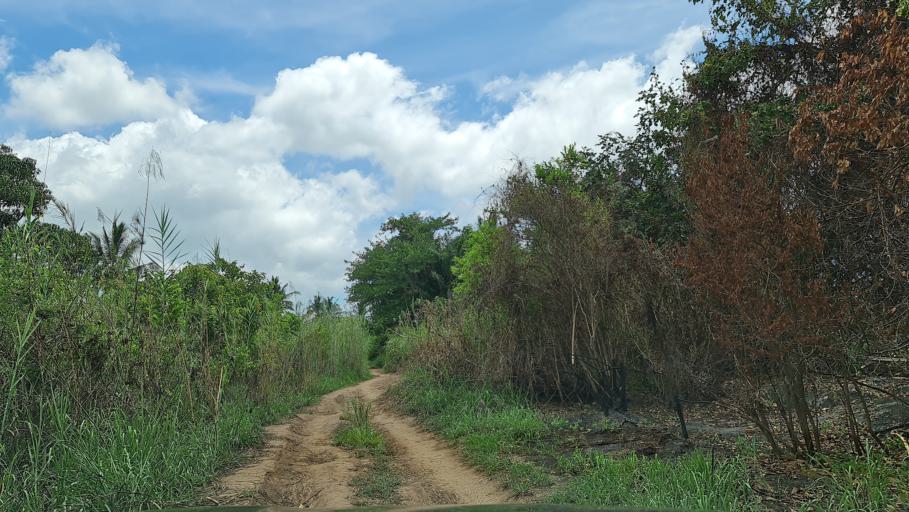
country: MZ
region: Zambezia
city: Quelimane
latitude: -17.5859
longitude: 37.3910
